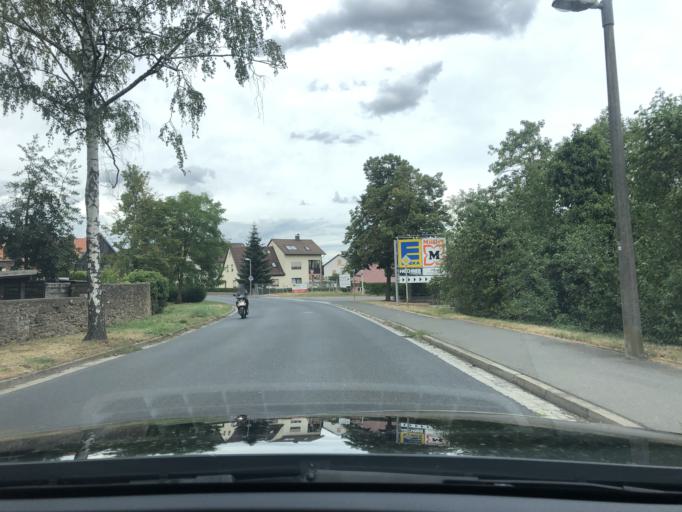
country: DE
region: Bavaria
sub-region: Regierungsbezirk Unterfranken
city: Hofheim in Unterfranken
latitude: 50.1355
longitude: 10.5252
